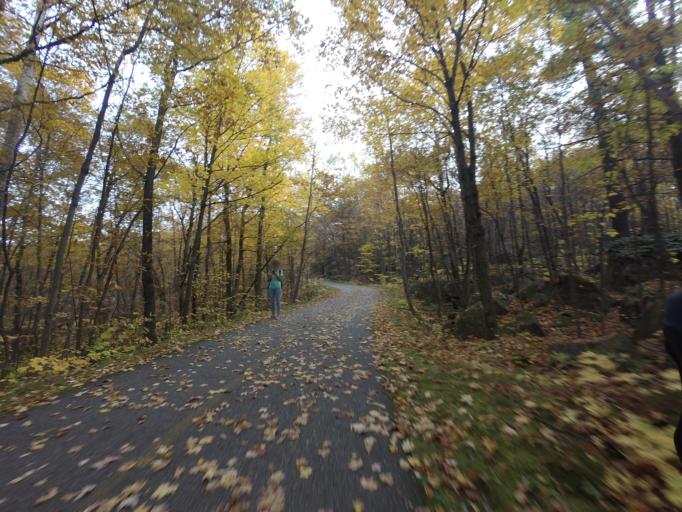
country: CA
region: Quebec
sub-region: Outaouais
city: Gatineau
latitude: 45.4580
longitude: -75.7800
